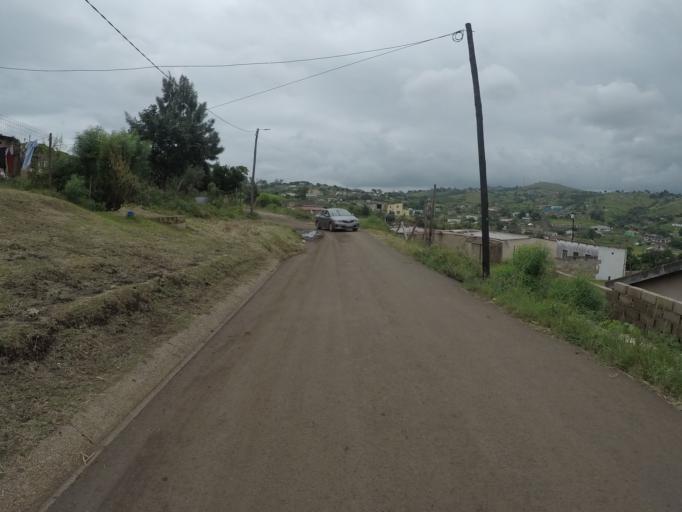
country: ZA
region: KwaZulu-Natal
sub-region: uThungulu District Municipality
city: Empangeni
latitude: -28.7665
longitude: 31.8555
